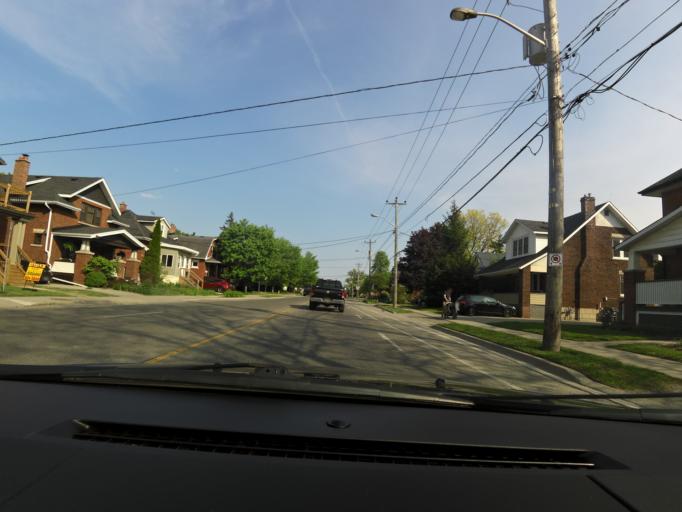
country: CA
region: Ontario
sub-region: Wellington County
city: Guelph
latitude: 43.5577
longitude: -80.2675
